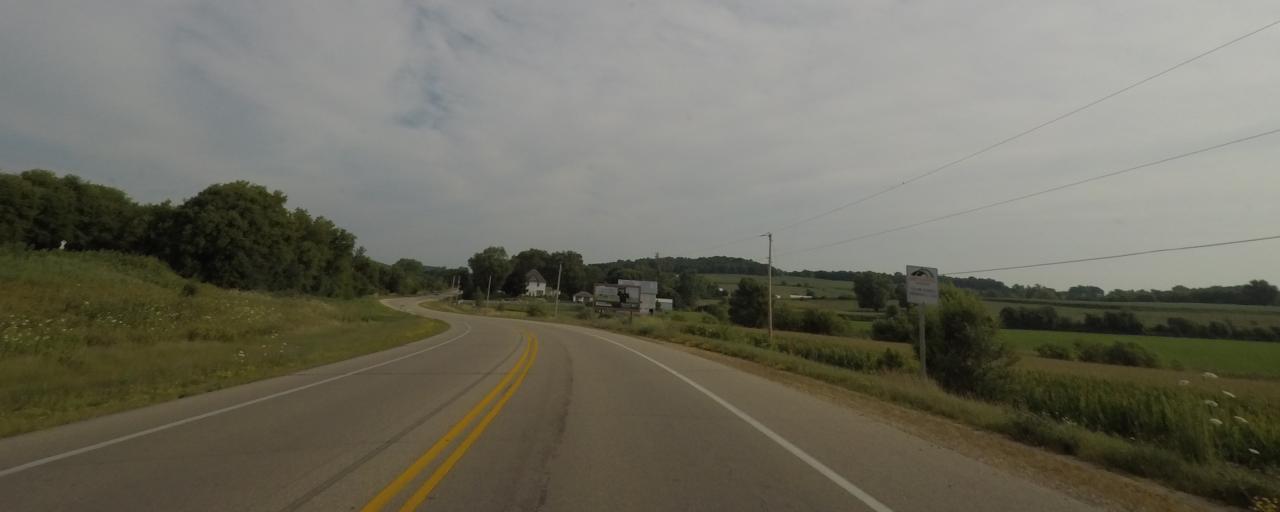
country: US
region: Wisconsin
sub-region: Columbia County
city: Lodi
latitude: 43.2945
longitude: -89.5219
